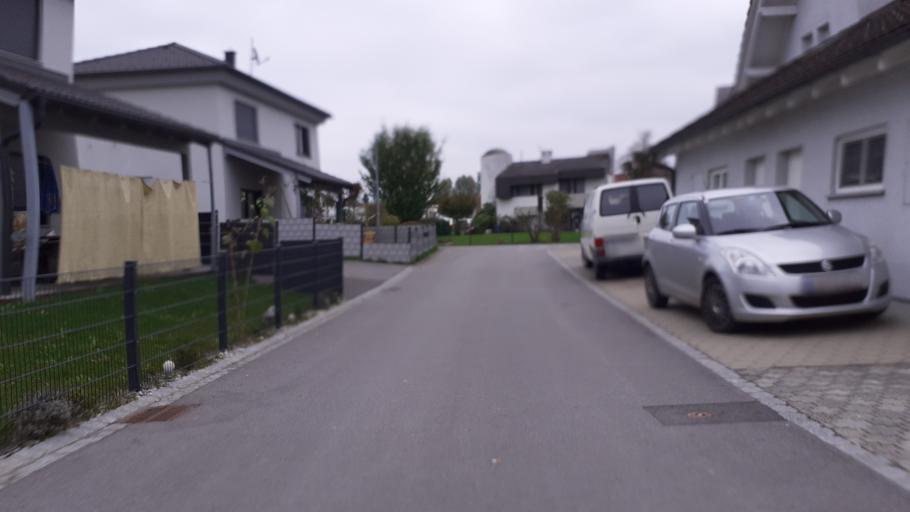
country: AT
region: Vorarlberg
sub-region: Politischer Bezirk Dornbirn
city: Lustenau
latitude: 47.4217
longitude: 9.6663
